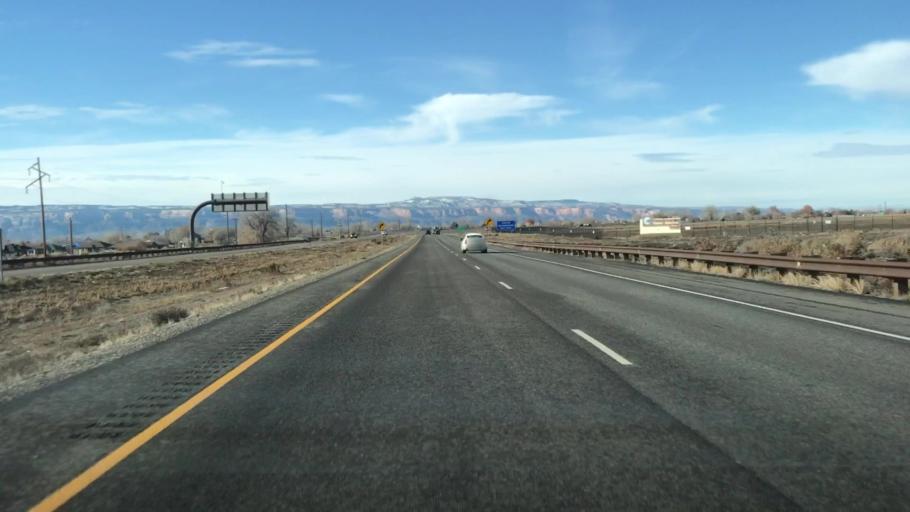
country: US
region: Colorado
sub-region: Mesa County
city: Fruitvale
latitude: 39.1060
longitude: -108.5248
